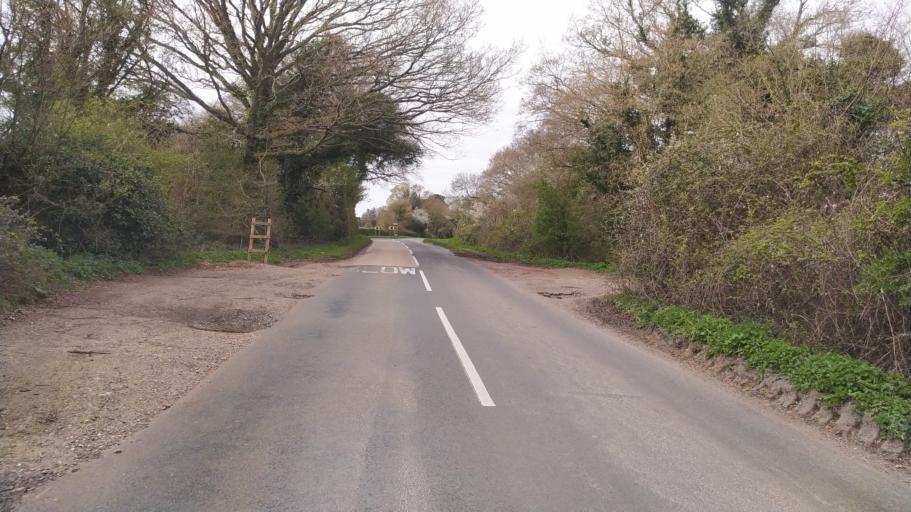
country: GB
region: England
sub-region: Hampshire
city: Bishops Waltham
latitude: 50.9780
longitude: -1.2066
